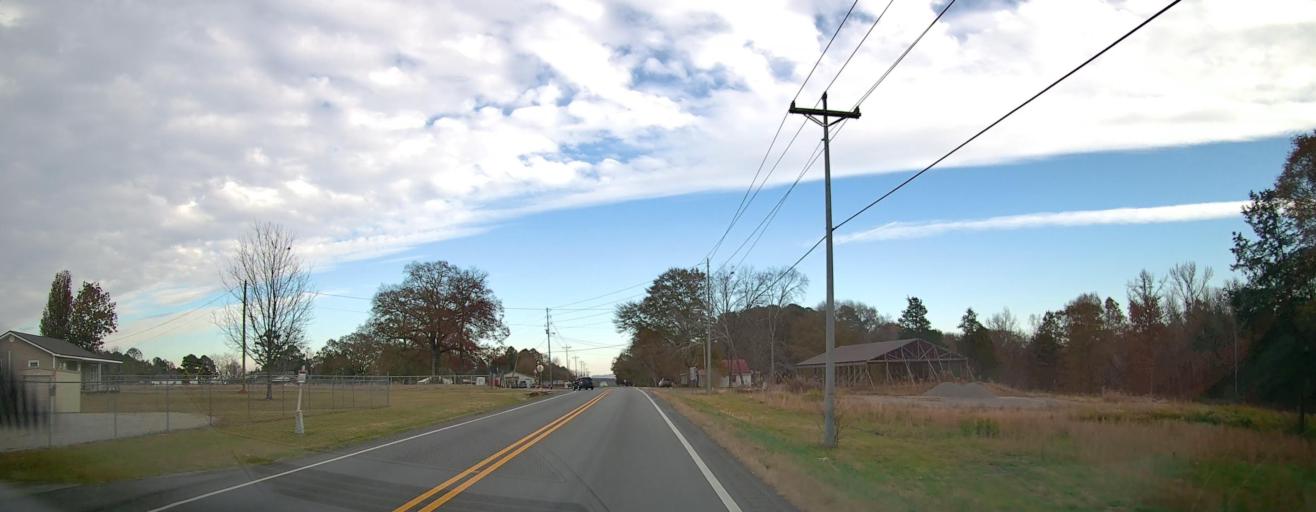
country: US
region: Alabama
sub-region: Morgan County
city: Priceville
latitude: 34.4737
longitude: -86.8063
